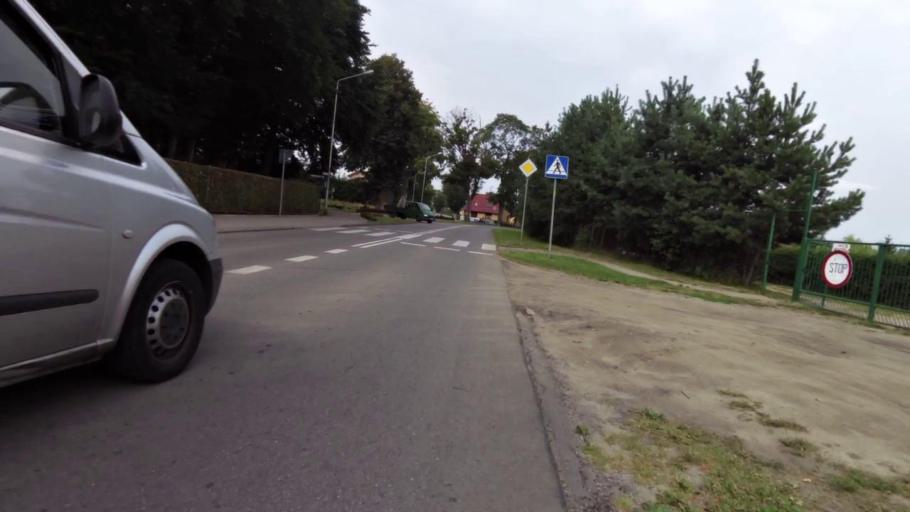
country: PL
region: West Pomeranian Voivodeship
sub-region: Powiat drawski
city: Drawsko Pomorskie
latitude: 53.5405
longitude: 15.8135
